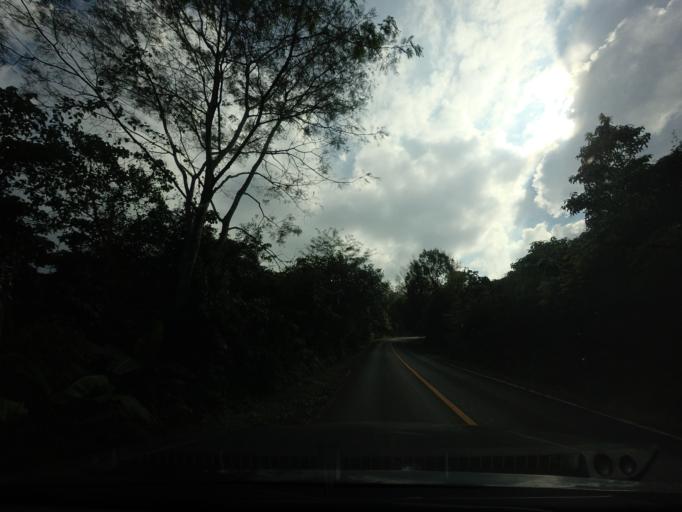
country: TH
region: Phitsanulok
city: Nakhon Thai
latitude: 16.9749
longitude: 101.0205
